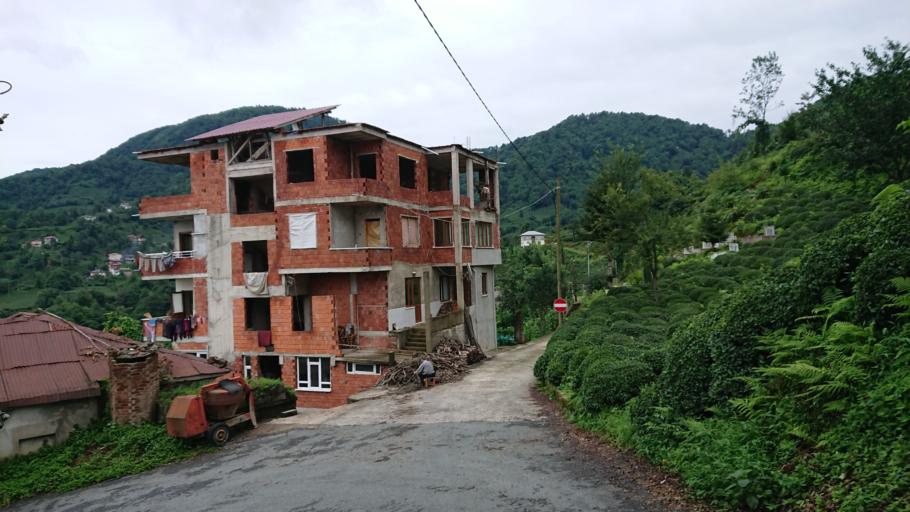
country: TR
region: Rize
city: Rize
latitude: 40.9811
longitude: 40.4855
